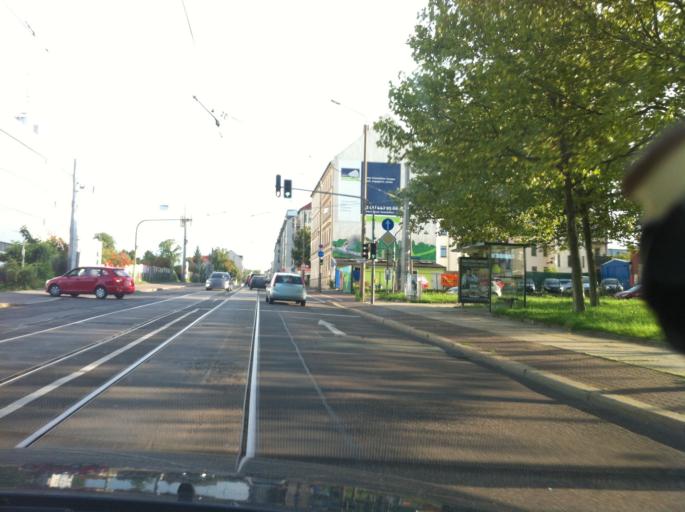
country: DE
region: Saxony
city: Markkleeberg
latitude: 51.3056
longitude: 12.3221
